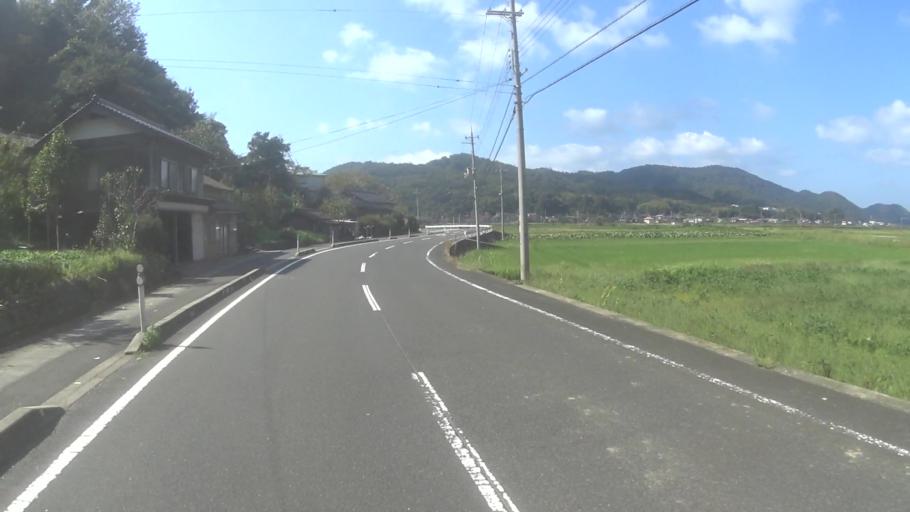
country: JP
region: Kyoto
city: Miyazu
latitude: 35.7129
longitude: 135.1111
